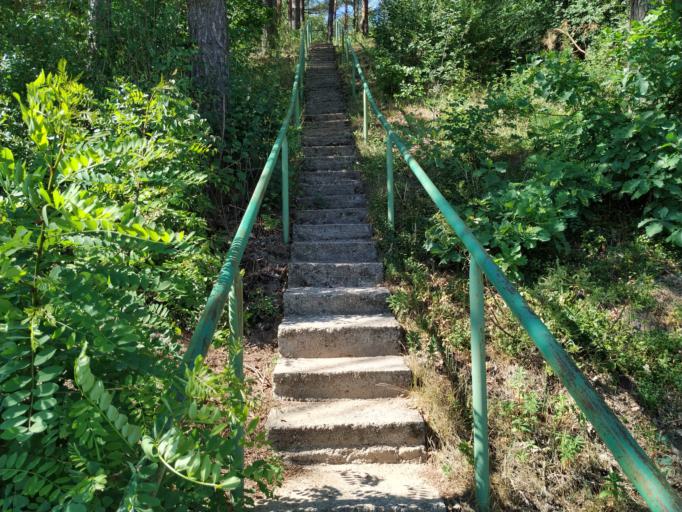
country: LT
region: Vilnius County
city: Rasos
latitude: 54.7603
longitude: 25.3469
